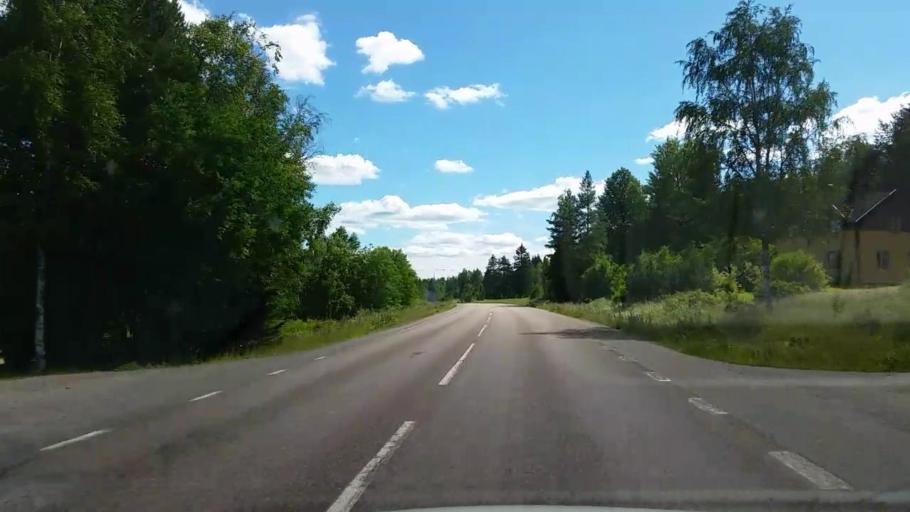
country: SE
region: Dalarna
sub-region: Faluns Kommun
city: Svardsjo
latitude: 60.8372
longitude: 15.7603
